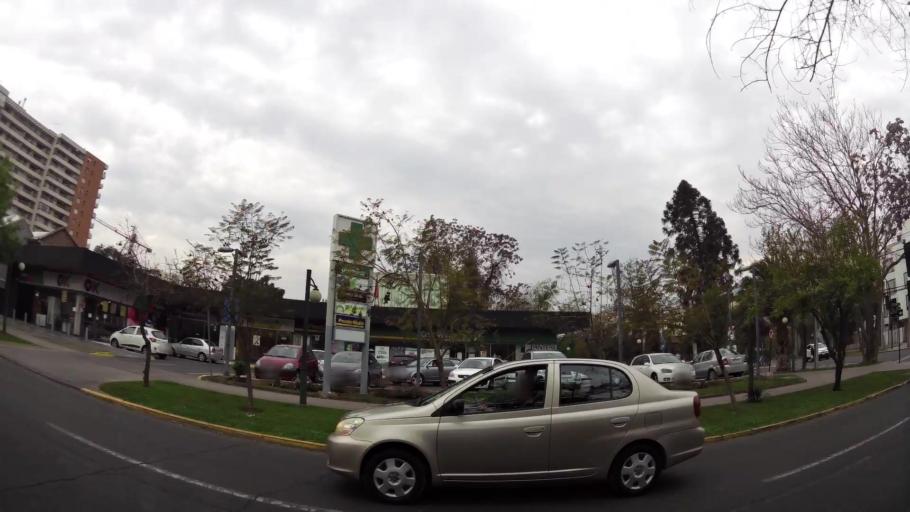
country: CL
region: Santiago Metropolitan
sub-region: Provincia de Santiago
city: Villa Presidente Frei, Nunoa, Santiago, Chile
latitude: -33.4483
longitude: -70.6107
